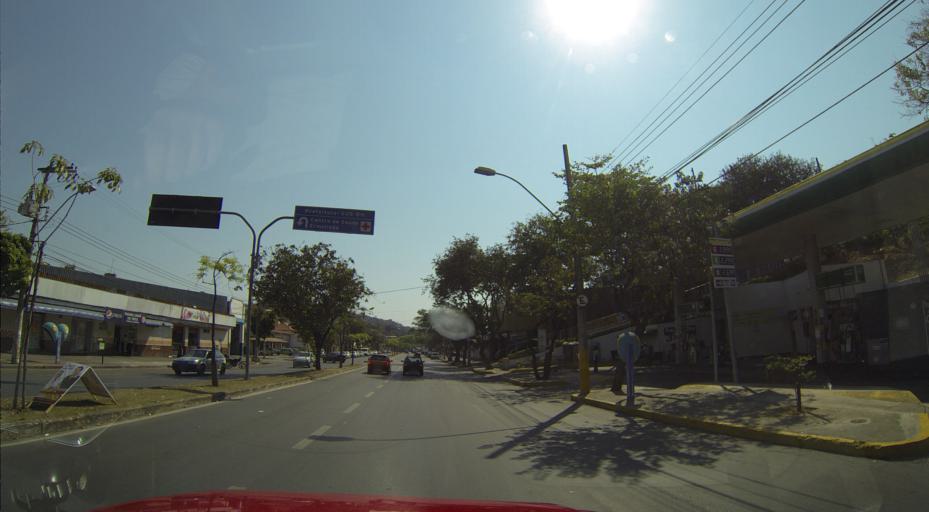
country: BR
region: Minas Gerais
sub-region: Belo Horizonte
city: Belo Horizonte
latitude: -19.8913
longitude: -43.9573
